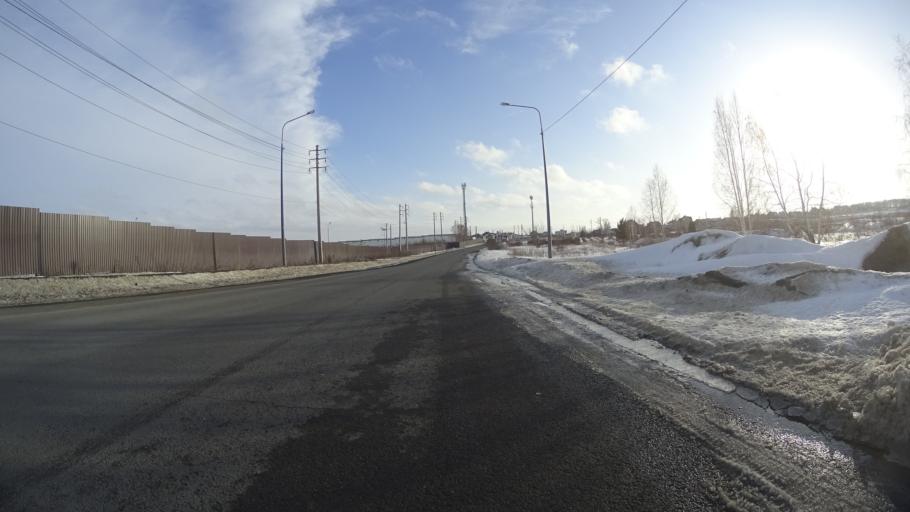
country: RU
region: Chelyabinsk
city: Sargazy
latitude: 55.1205
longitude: 61.2868
